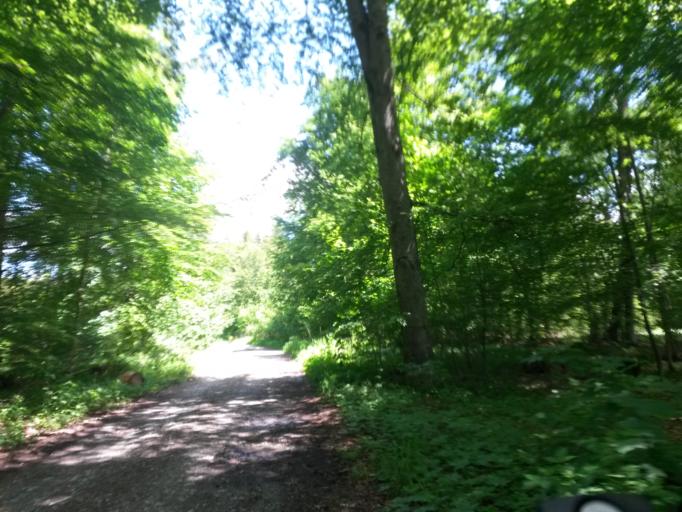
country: DE
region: Baden-Wuerttemberg
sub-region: Tuebingen Region
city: Aulendorf
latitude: 47.9551
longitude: 9.6775
